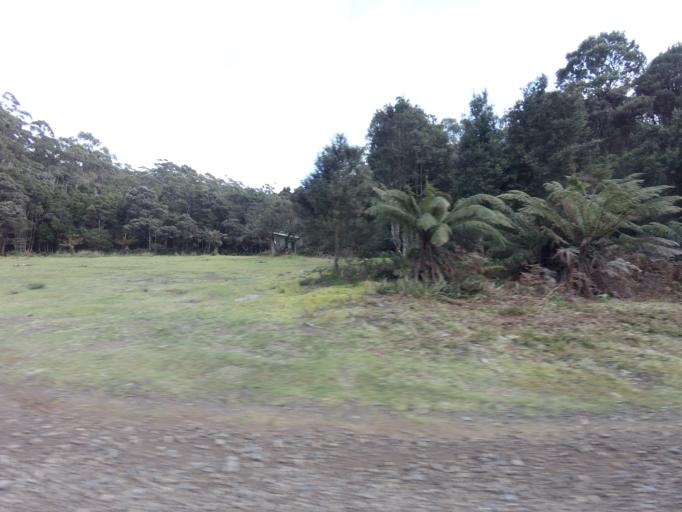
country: AU
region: Tasmania
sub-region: Huon Valley
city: Geeveston
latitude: -43.5435
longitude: 146.8906
